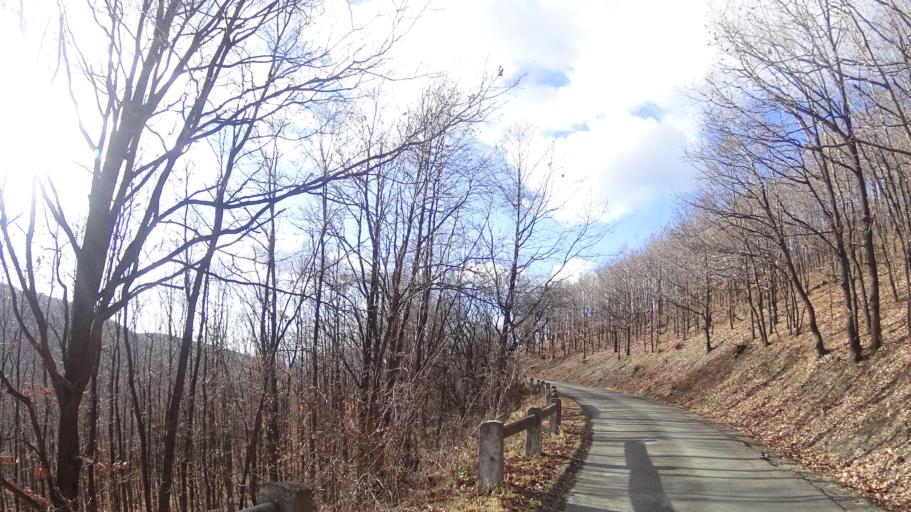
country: HU
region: Heves
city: Szilvasvarad
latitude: 48.0948
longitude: 20.4040
